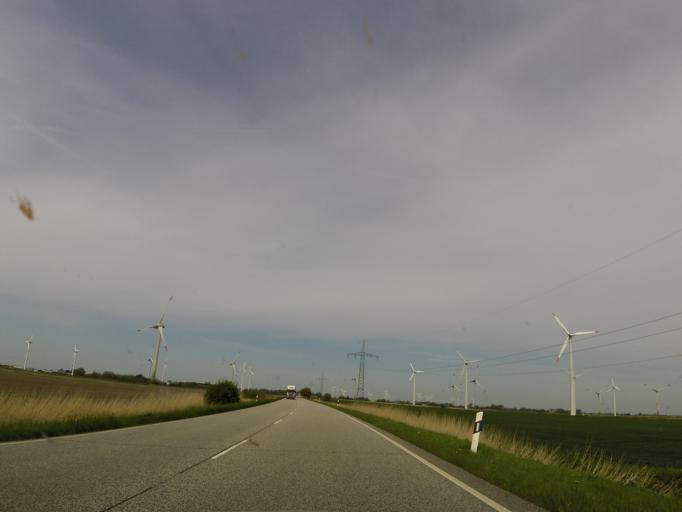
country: DE
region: Schleswig-Holstein
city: Stelle-Wittenwurth
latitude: 54.2627
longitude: 9.0325
